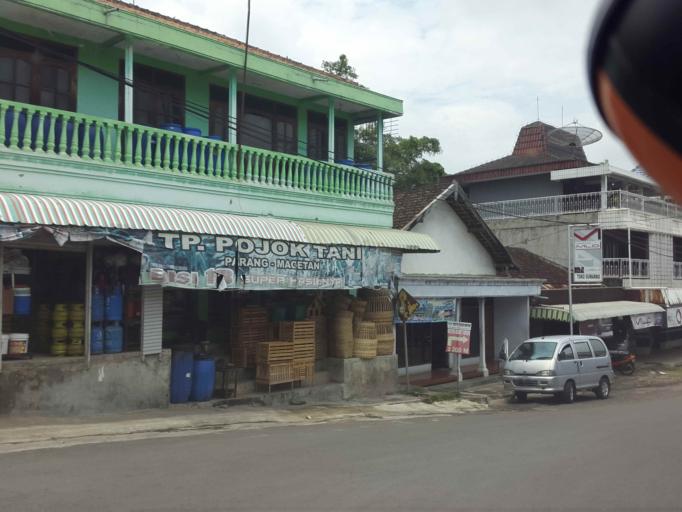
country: ID
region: East Java
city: Ponorogo
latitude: -7.7479
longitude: 111.3305
